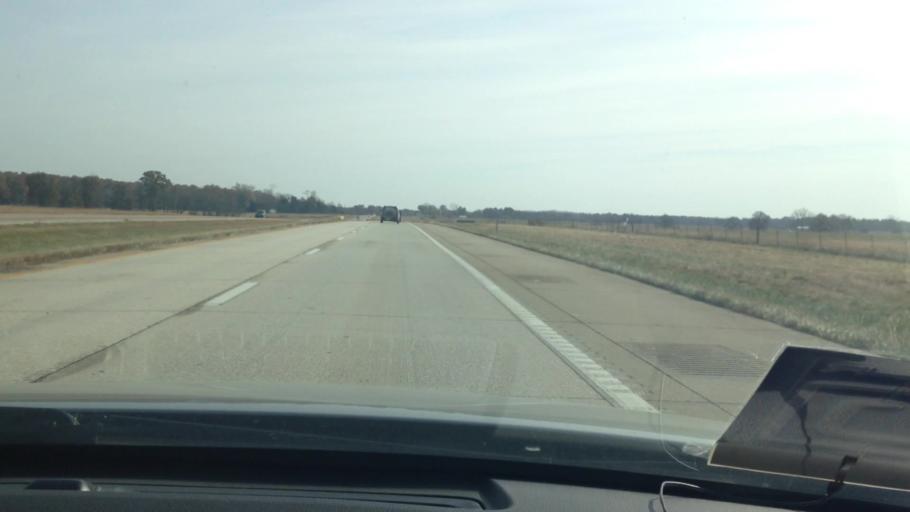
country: US
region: Missouri
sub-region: Henry County
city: Clinton
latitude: 38.4099
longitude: -93.8517
